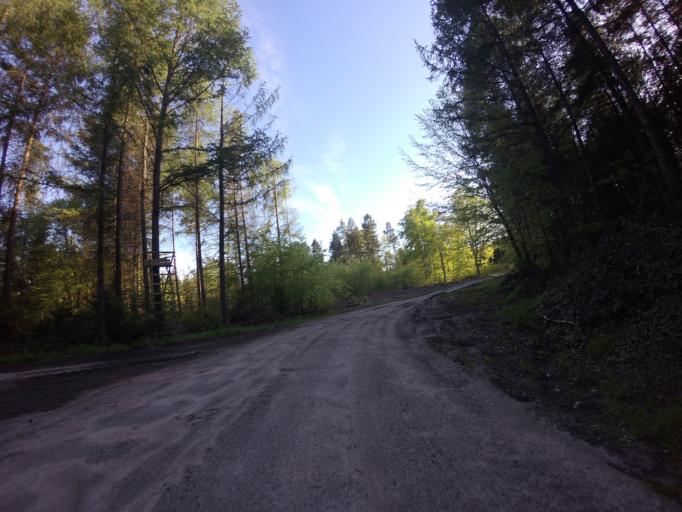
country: PL
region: West Pomeranian Voivodeship
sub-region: Powiat choszczenski
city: Drawno
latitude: 53.2186
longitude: 15.6824
